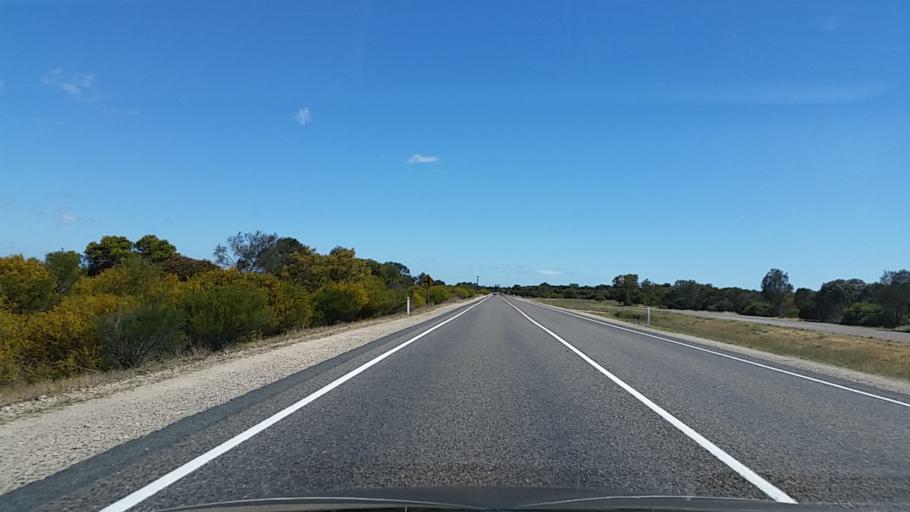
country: AU
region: South Australia
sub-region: Murray Bridge
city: Tailem Bend
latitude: -35.2895
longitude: 139.4468
